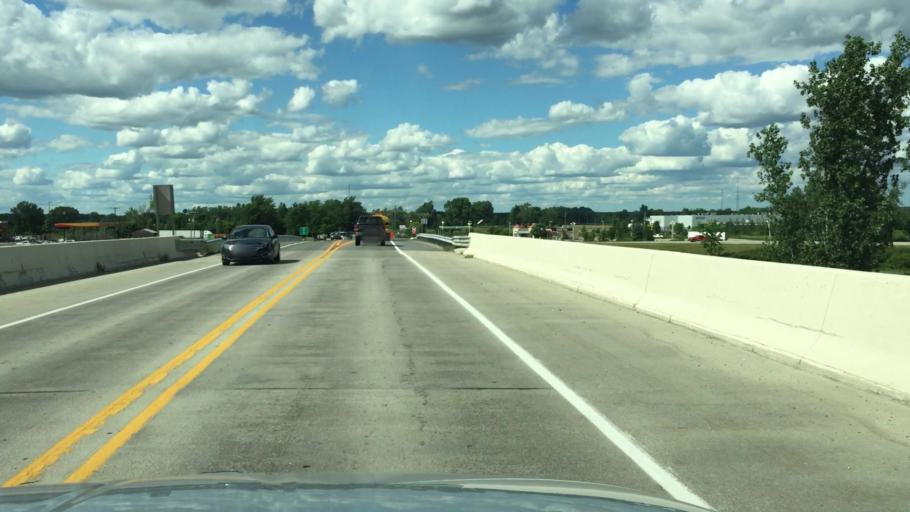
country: US
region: Michigan
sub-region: Saint Clair County
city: Capac
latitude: 42.9867
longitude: -82.9277
